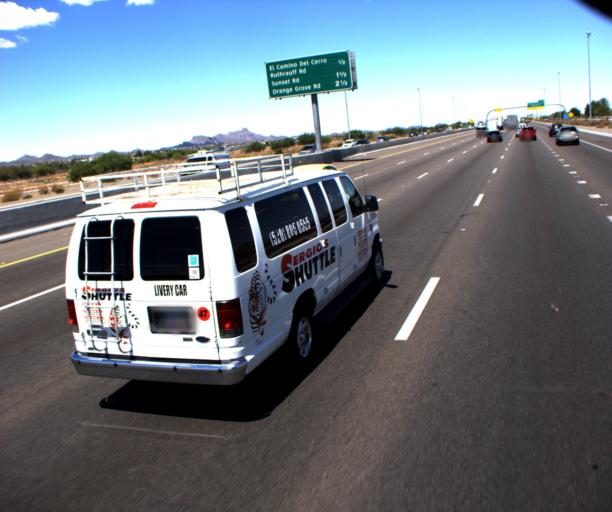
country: US
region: Arizona
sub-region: Pima County
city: Flowing Wells
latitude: 32.2822
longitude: -111.0191
